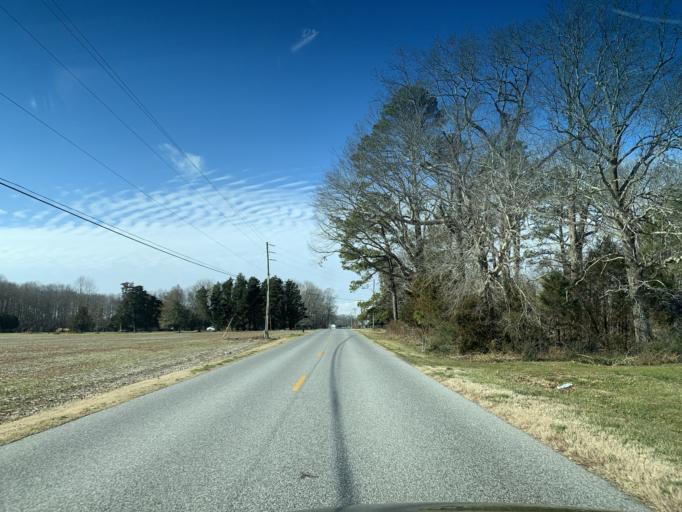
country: US
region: Maryland
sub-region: Worcester County
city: Ocean Pines
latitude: 38.4195
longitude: -75.1481
